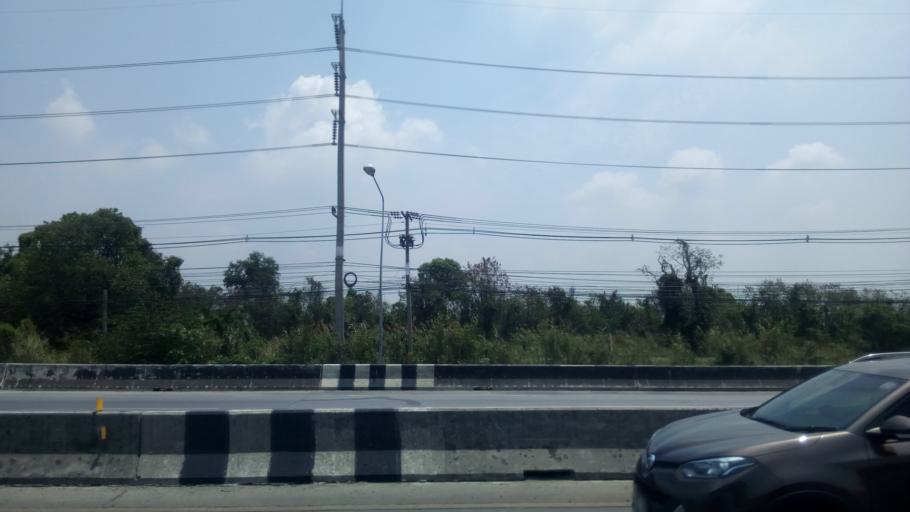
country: TH
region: Pathum Thani
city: Pathum Thani
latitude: 14.0280
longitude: 100.5366
